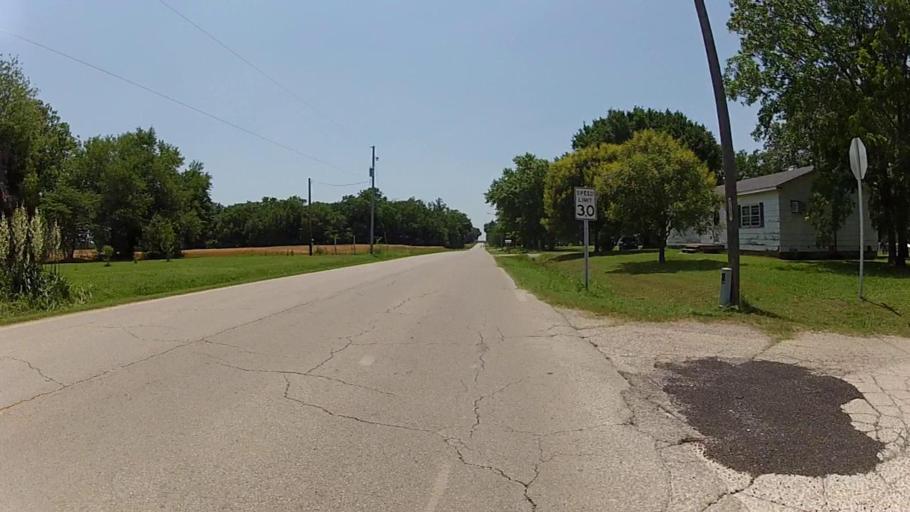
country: US
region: Kansas
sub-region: Montgomery County
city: Cherryvale
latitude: 37.2634
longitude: -95.5370
